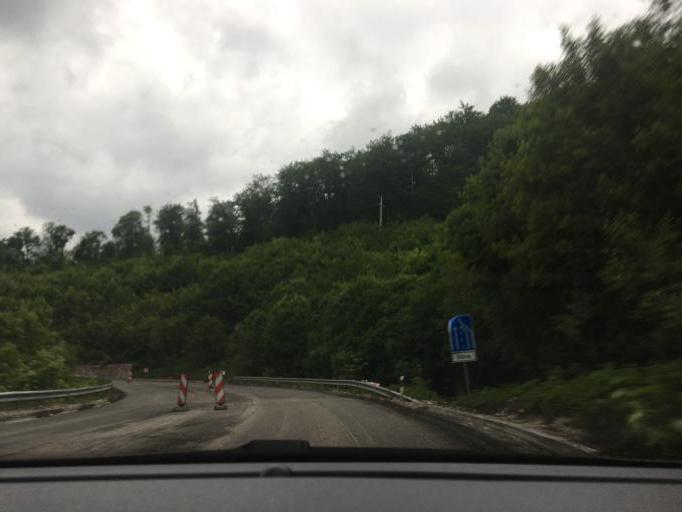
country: MK
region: Gostivar
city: Vrutok
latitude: 41.6685
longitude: 20.8560
